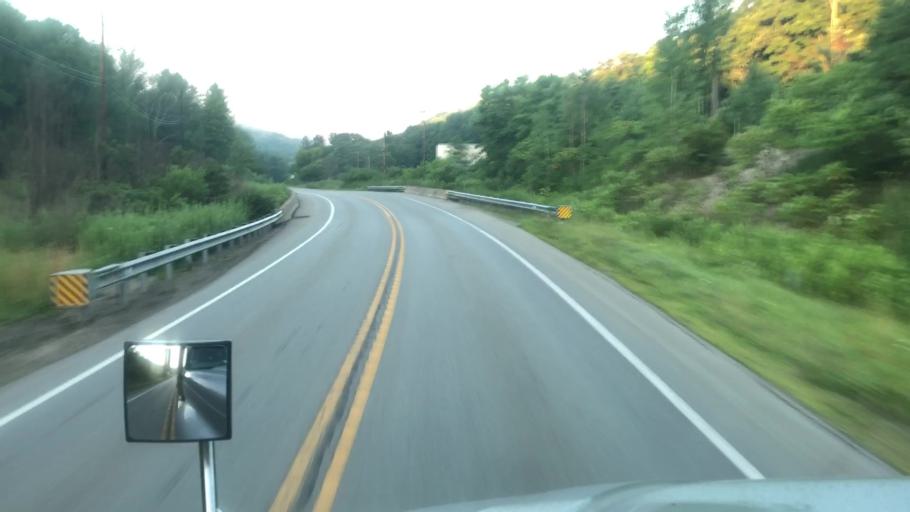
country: US
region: Pennsylvania
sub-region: Venango County
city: Hasson Heights
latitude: 41.4793
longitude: -79.6779
